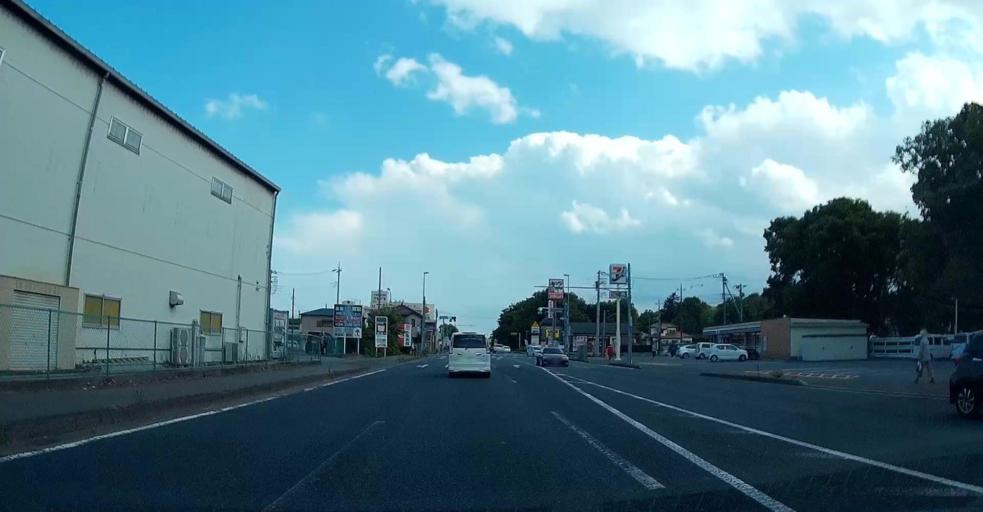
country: JP
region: Chiba
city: Noda
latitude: 35.9544
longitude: 139.8768
